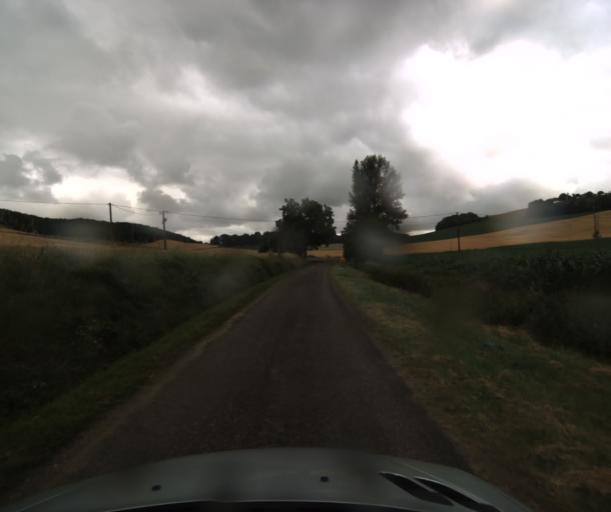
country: FR
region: Midi-Pyrenees
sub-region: Departement du Tarn-et-Garonne
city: Lavit
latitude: 43.9467
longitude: 0.9414
